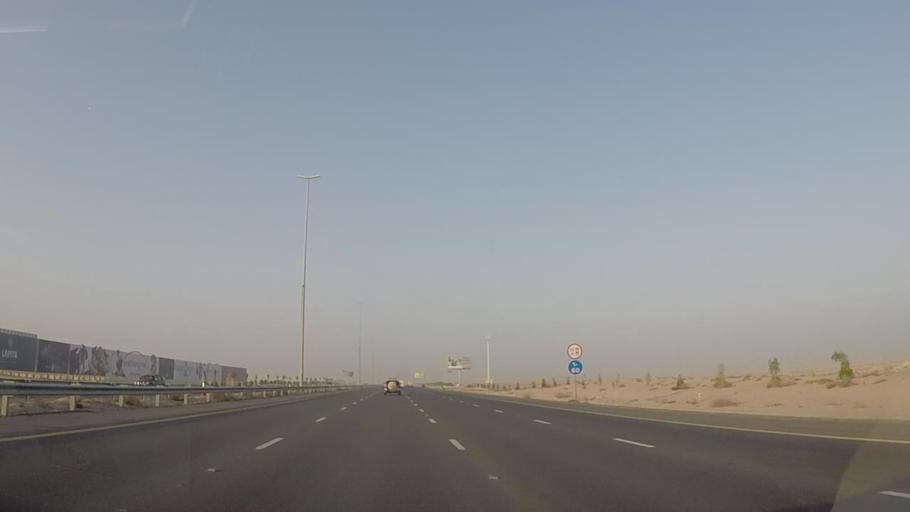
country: AE
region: Dubai
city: Dubai
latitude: 24.9153
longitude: 54.9702
